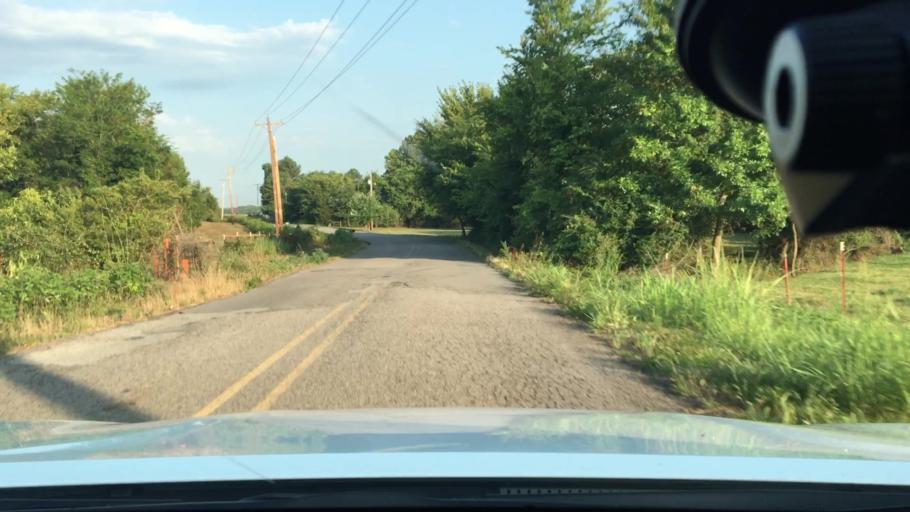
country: US
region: Arkansas
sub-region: Johnson County
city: Coal Hill
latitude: 35.3661
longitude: -93.5949
